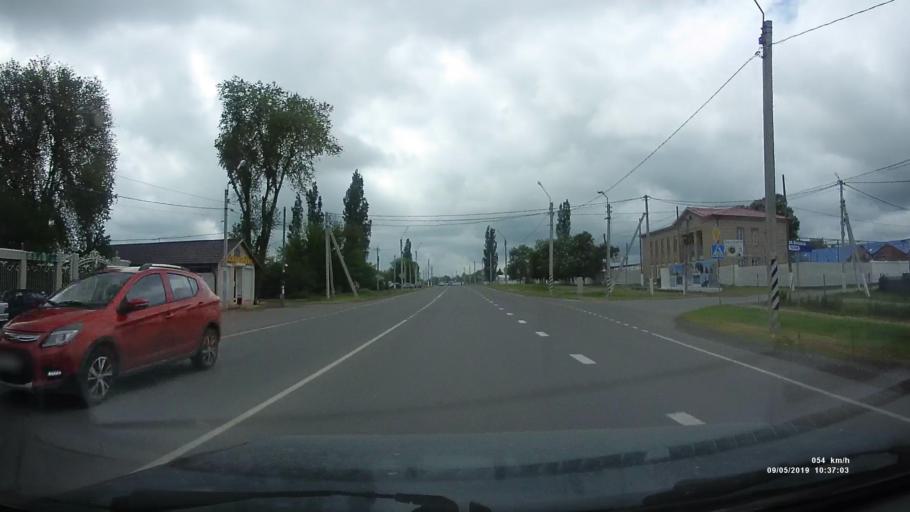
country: RU
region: Rostov
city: Peshkovo
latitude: 47.0234
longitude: 39.4047
